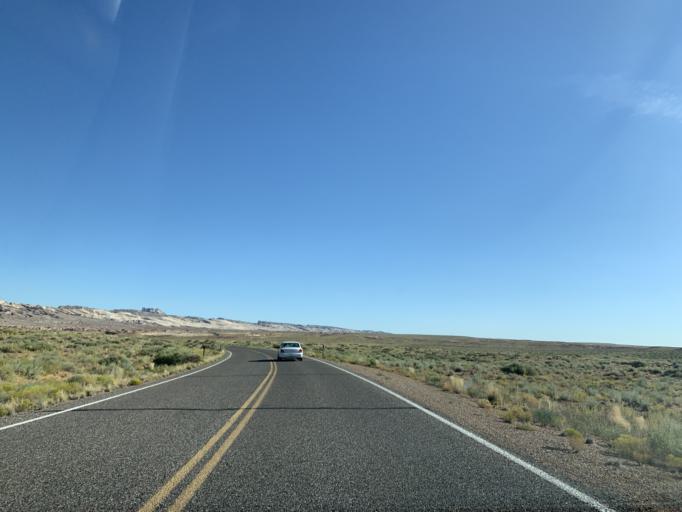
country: US
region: Utah
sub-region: Emery County
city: Ferron
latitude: 38.5736
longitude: -110.7071
